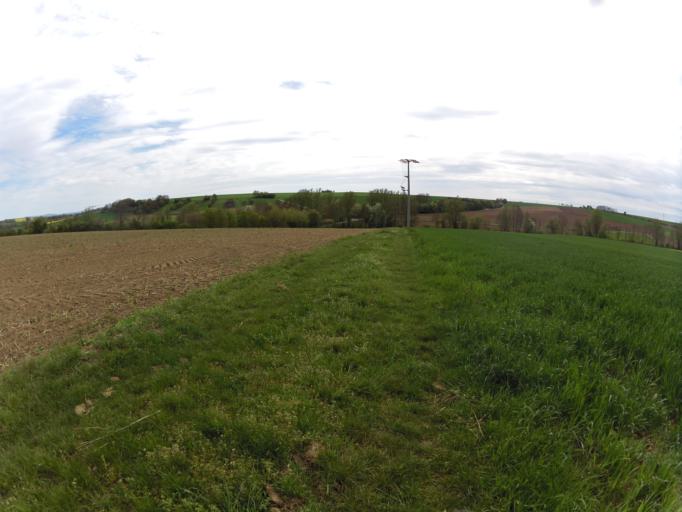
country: DE
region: Bavaria
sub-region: Regierungsbezirk Unterfranken
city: Prosselsheim
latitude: 49.8593
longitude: 10.1383
